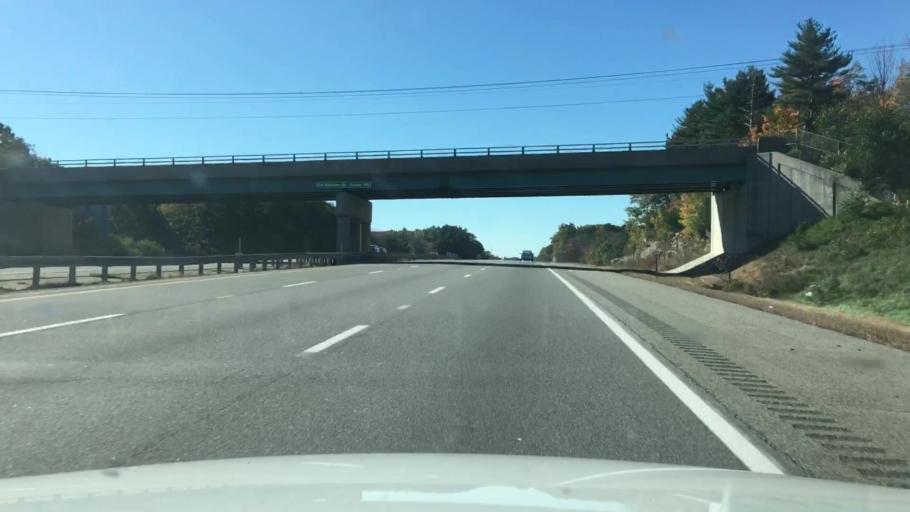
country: US
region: Maine
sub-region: York County
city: West Kennebunk
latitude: 43.3971
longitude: -70.5673
